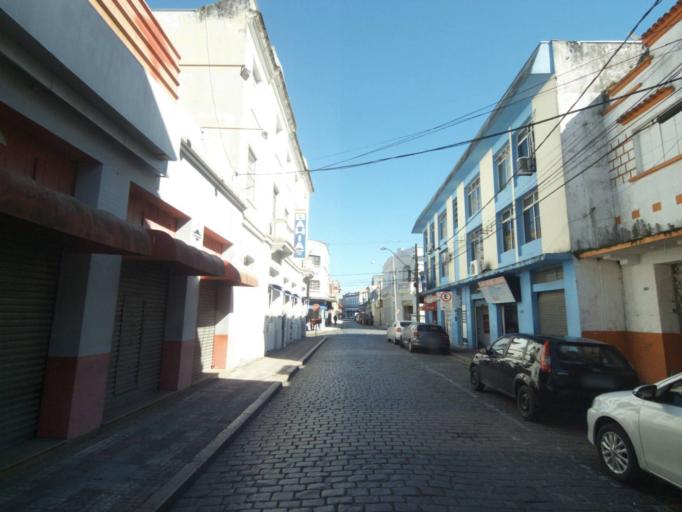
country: BR
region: Parana
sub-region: Paranagua
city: Paranagua
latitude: -25.5196
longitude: -48.5052
